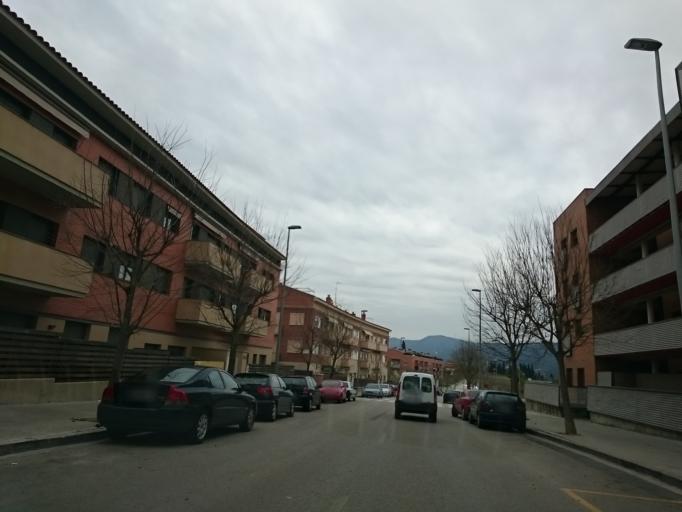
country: ES
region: Catalonia
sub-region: Provincia de Barcelona
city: Sant Sadurni d'Anoia
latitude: 41.4302
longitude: 1.7877
